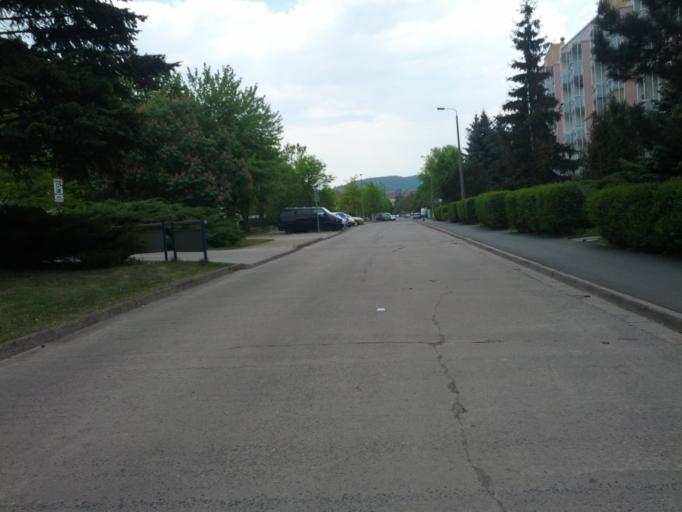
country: DE
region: Thuringia
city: Eisenach
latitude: 50.9974
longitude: 10.3126
